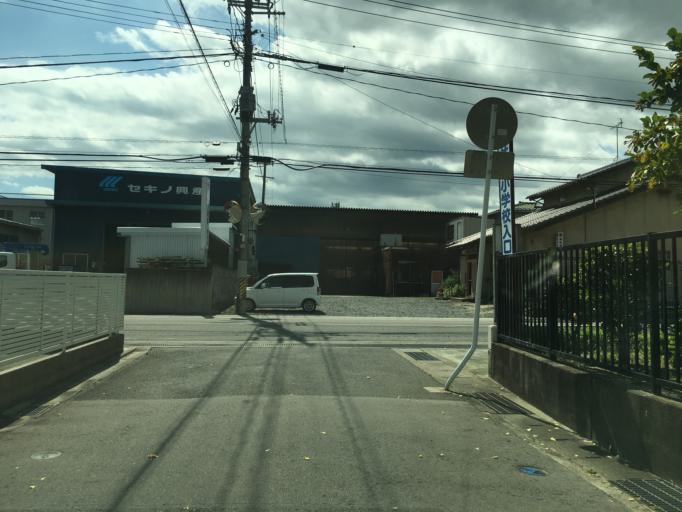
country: JP
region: Fukushima
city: Fukushima-shi
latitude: 37.7442
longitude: 140.4331
